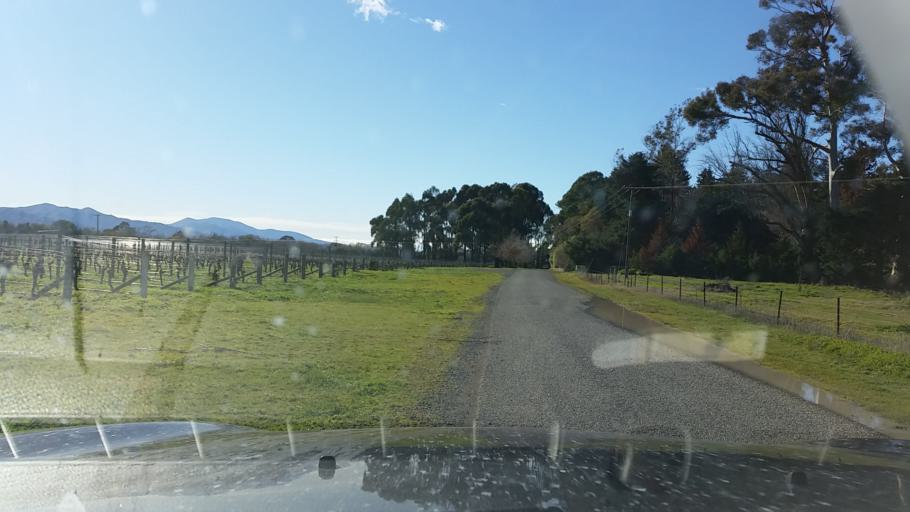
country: NZ
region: Marlborough
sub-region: Marlborough District
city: Blenheim
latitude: -41.5275
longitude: 173.8075
